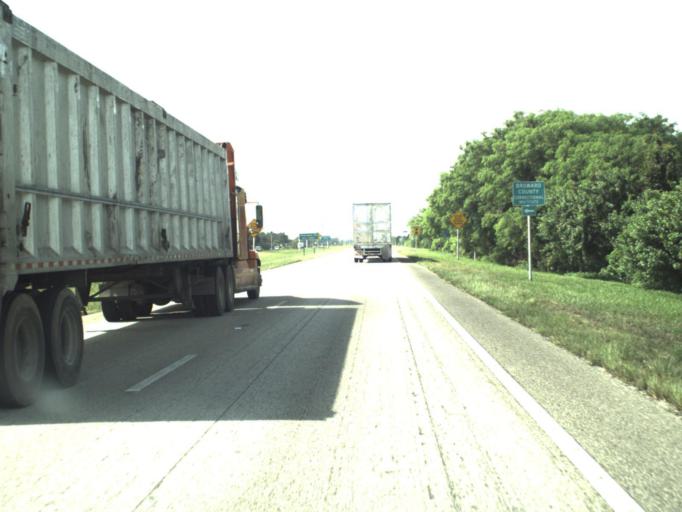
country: US
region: Florida
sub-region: Broward County
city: Weston
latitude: 26.0333
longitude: -80.4337
